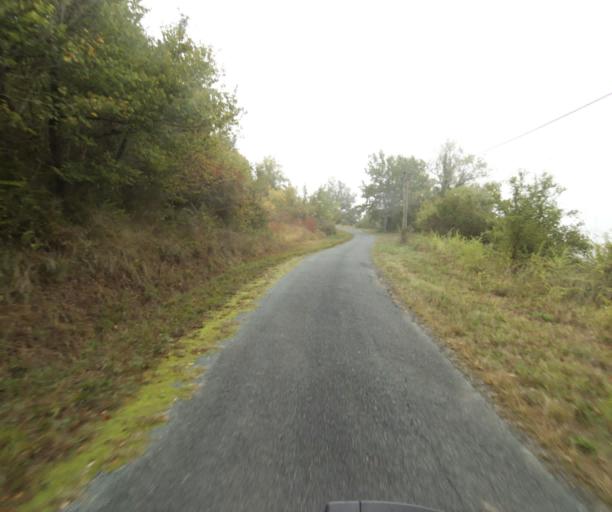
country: FR
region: Midi-Pyrenees
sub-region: Departement de la Haute-Garonne
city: Villemur-sur-Tarn
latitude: 43.8894
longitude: 1.4847
